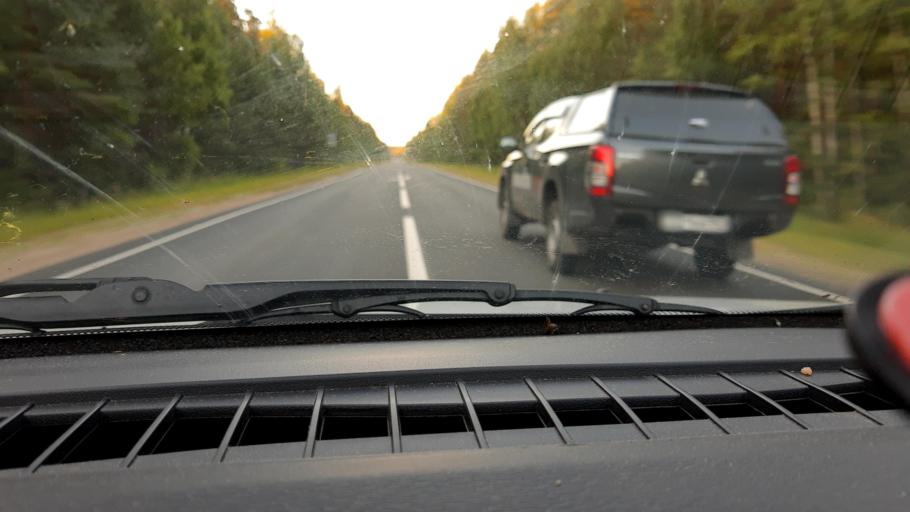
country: RU
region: Nizjnij Novgorod
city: Krasnyye Baki
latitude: 57.1668
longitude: 45.3102
